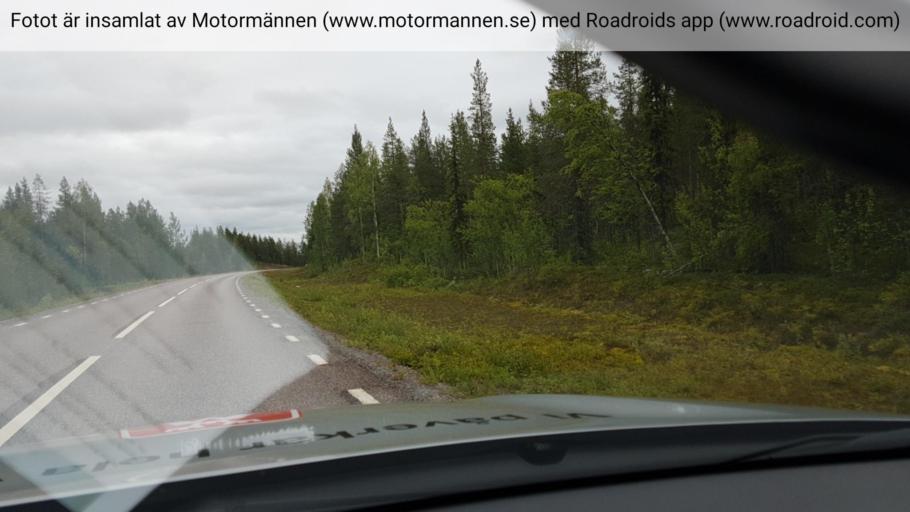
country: SE
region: Norrbotten
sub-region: Gallivare Kommun
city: Gaellivare
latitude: 67.0704
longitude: 21.5448
